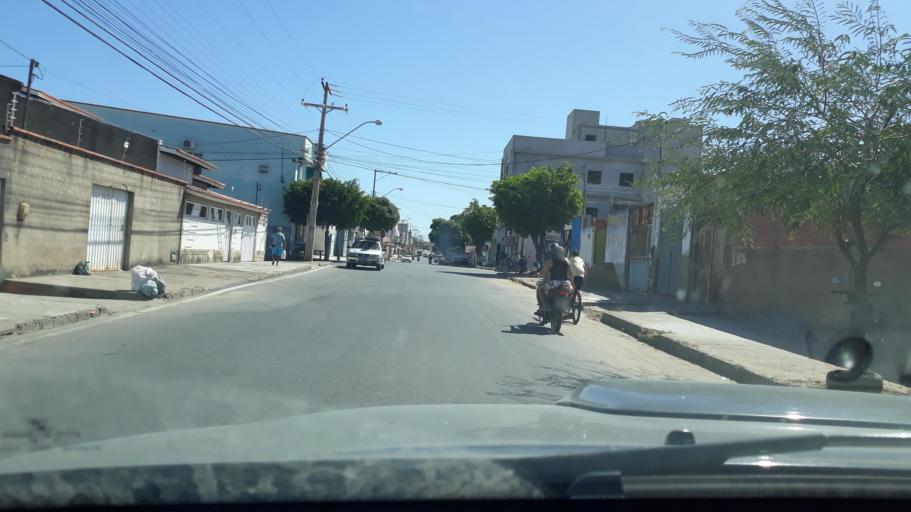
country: BR
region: Bahia
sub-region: Guanambi
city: Guanambi
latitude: -14.2221
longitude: -42.7920
